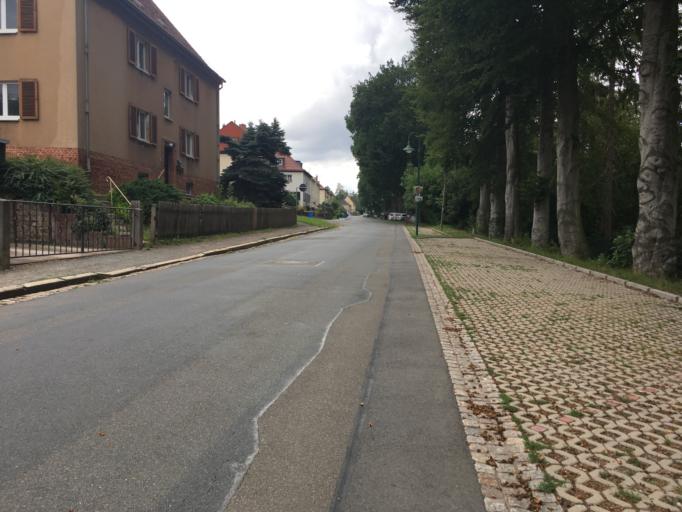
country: DE
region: Saxony
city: Crimmitschau
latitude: 50.8275
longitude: 12.3837
